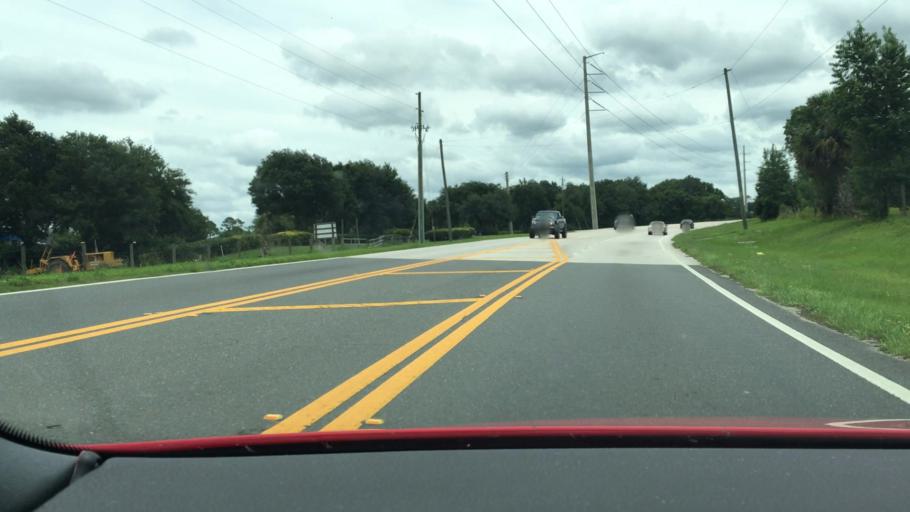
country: US
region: Florida
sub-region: Lake County
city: Eustis
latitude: 28.8749
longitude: -81.6695
